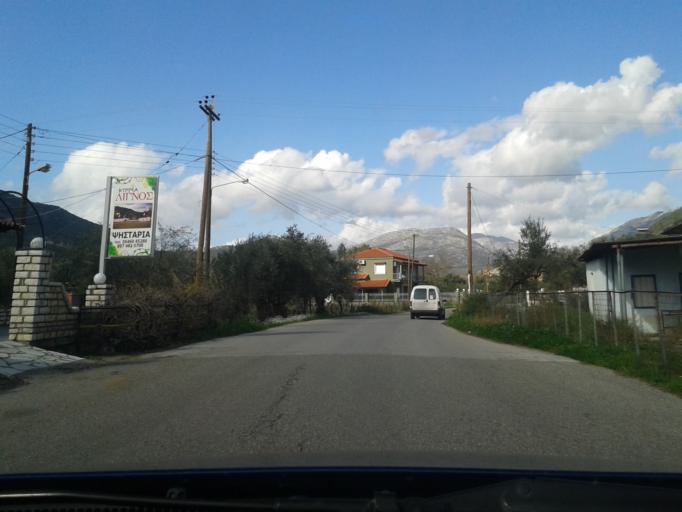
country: GR
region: West Greece
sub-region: Nomos Aitolias kai Akarnanias
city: Astakos
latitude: 38.5786
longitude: 21.0906
